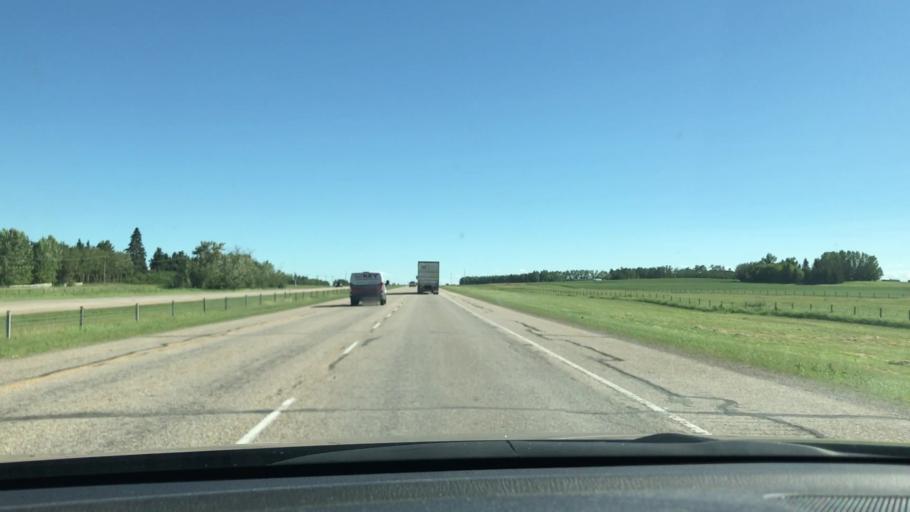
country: CA
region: Alberta
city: Olds
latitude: 51.8904
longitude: -114.0256
